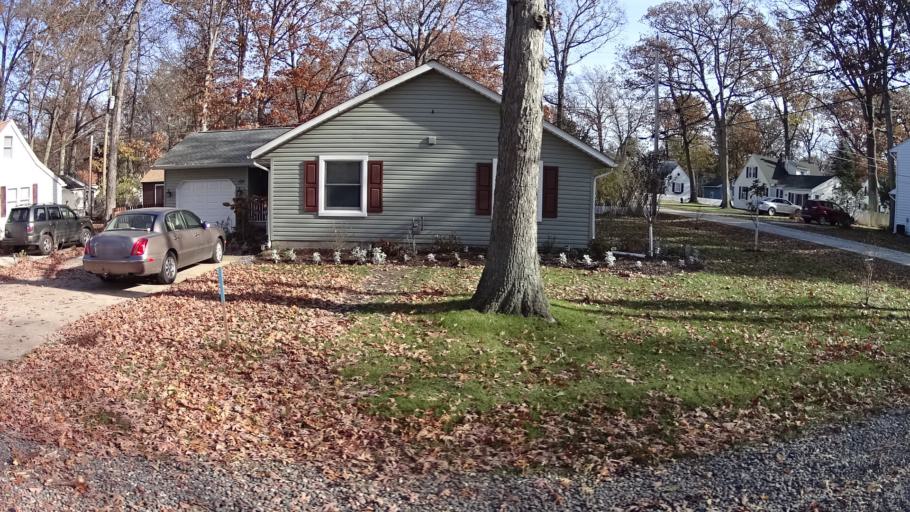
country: US
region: Ohio
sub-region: Lorain County
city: Avon Lake
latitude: 41.5042
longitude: -81.9842
